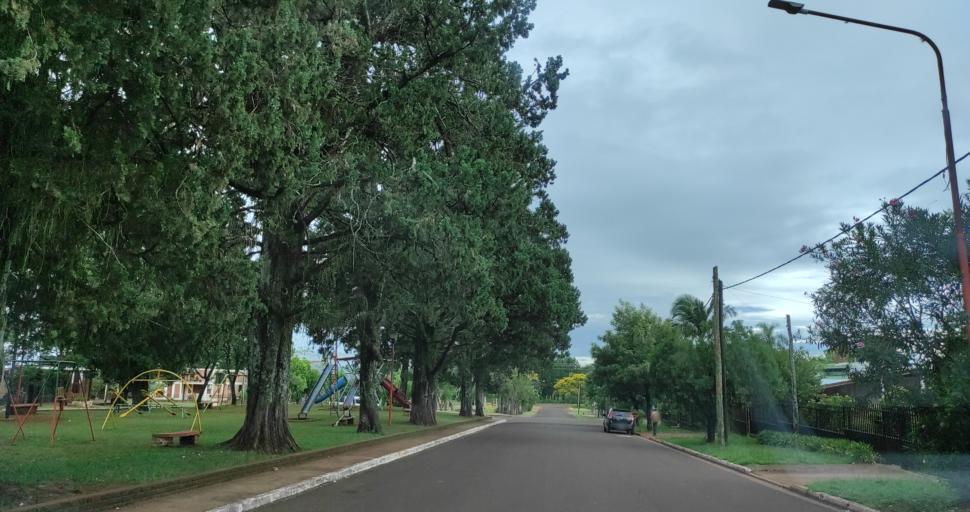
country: AR
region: Misiones
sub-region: Departamento de Apostoles
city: San Jose
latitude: -27.7675
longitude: -55.7772
